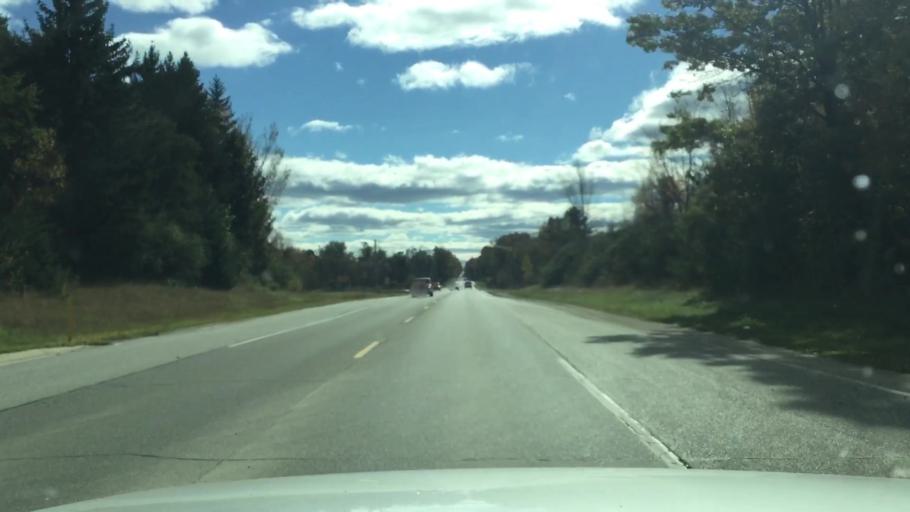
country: US
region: Michigan
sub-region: Lapeer County
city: Barnes Lake-Millers Lake
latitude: 43.1627
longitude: -83.3117
